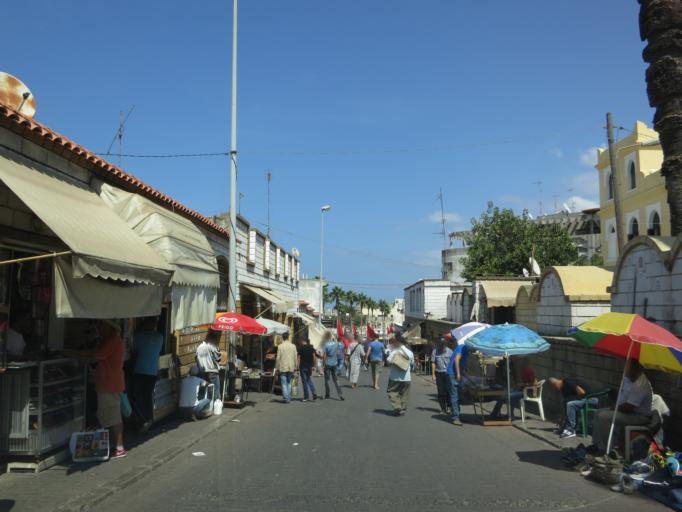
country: MA
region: Tanger-Tetouan
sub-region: Tanger-Assilah
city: Tangier
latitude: 35.7836
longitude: -5.8141
